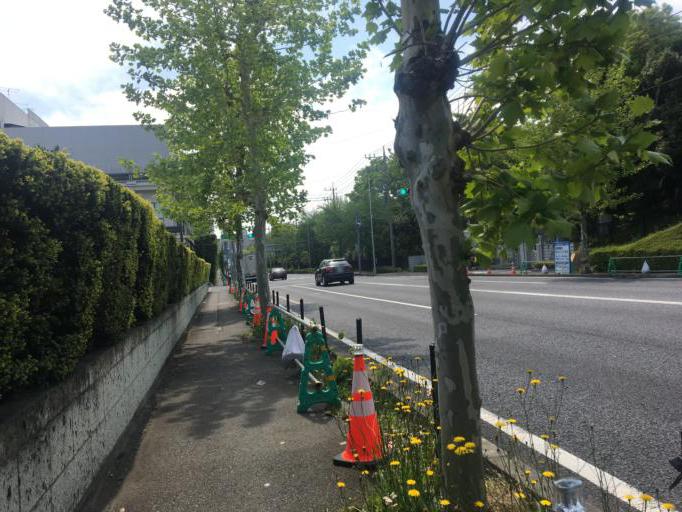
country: JP
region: Saitama
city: Wako
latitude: 35.7812
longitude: 139.6142
